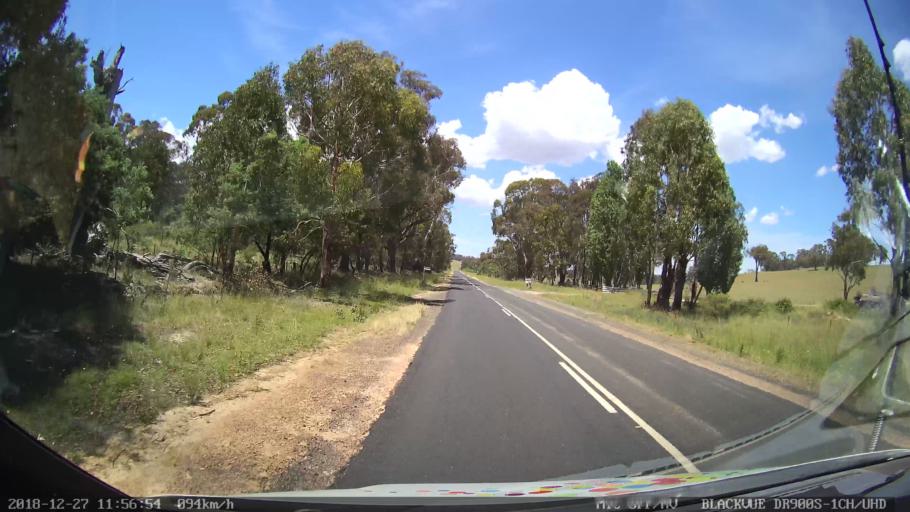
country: AU
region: New South Wales
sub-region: Blayney
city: Blayney
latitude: -33.7040
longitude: 149.3876
